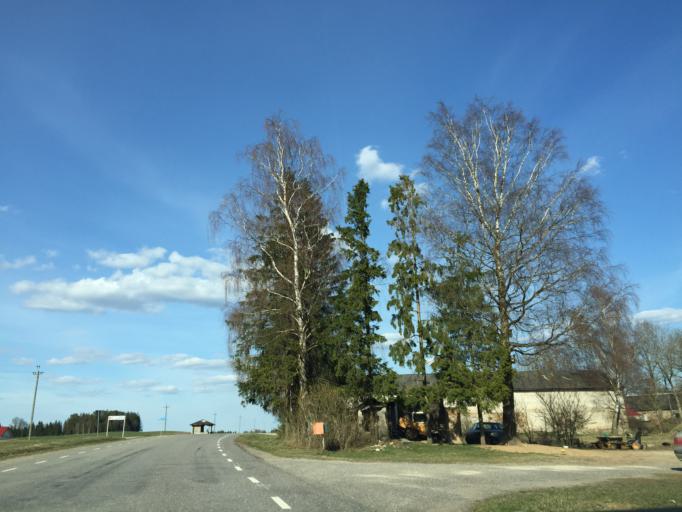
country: EE
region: Tartu
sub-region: Elva linn
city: Elva
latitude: 58.0754
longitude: 26.5225
